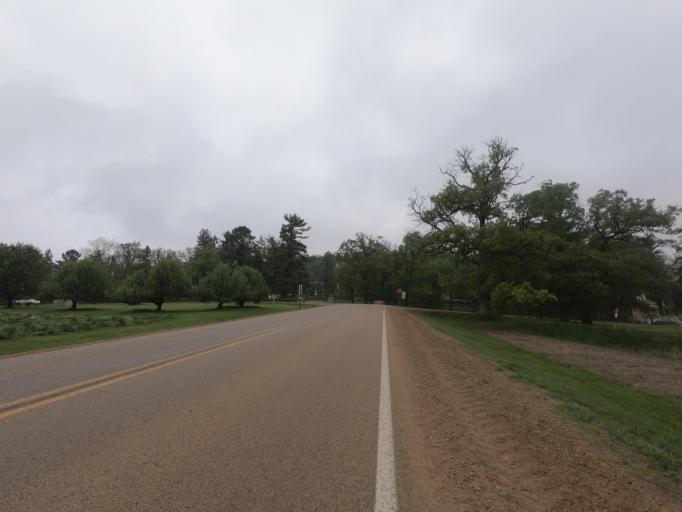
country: US
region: Illinois
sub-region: Jo Daviess County
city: East Dubuque
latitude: 42.5214
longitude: -90.5441
